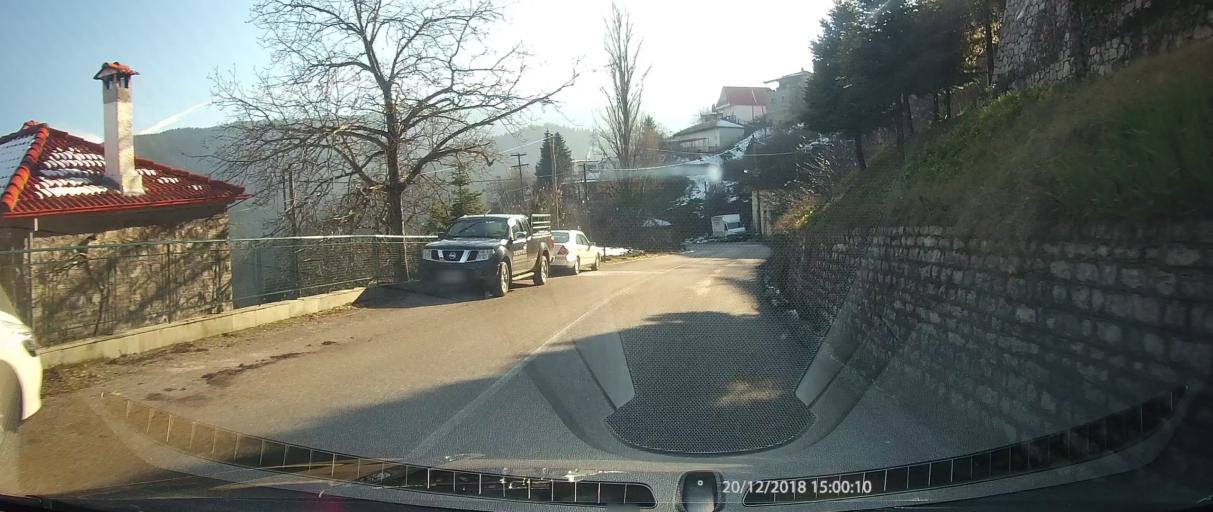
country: GR
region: Central Greece
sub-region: Nomos Evrytanias
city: Karpenisi
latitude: 38.9096
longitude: 21.9168
